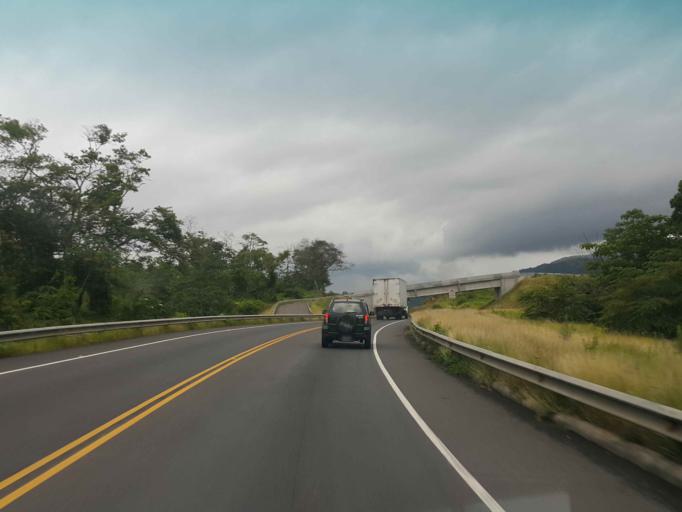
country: CR
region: Alajuela
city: Atenas
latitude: 9.9423
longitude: -84.3965
